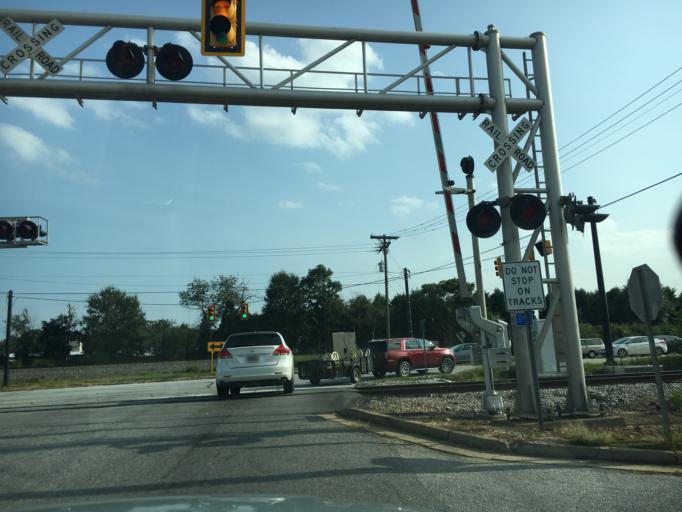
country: US
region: South Carolina
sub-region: Greenville County
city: Wade Hampton
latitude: 34.9034
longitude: -82.3503
